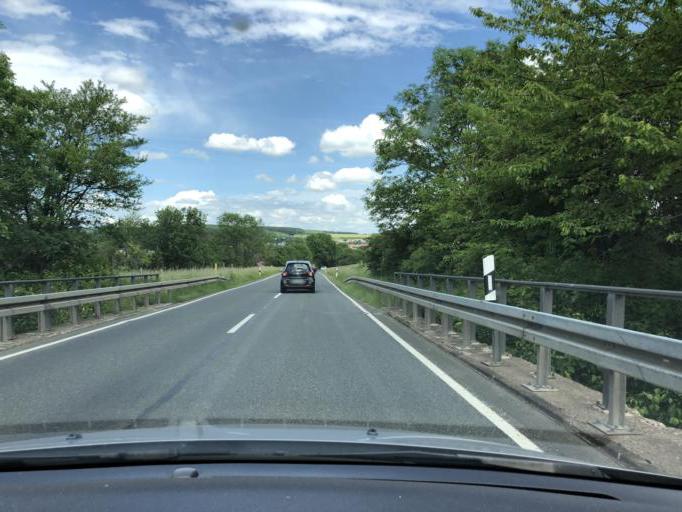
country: DE
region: Thuringia
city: Kefferhausen
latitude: 51.3100
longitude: 10.2997
